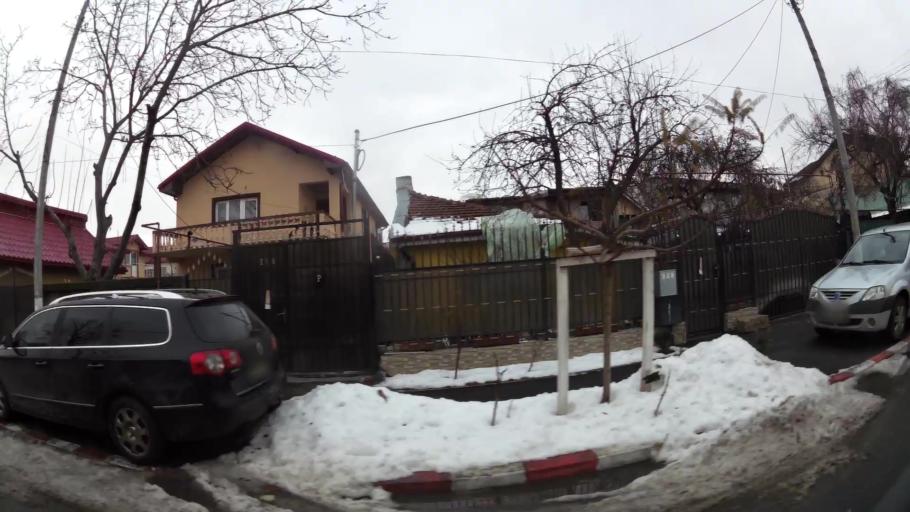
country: RO
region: Ilfov
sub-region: Voluntari City
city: Voluntari
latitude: 44.4881
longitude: 26.1749
